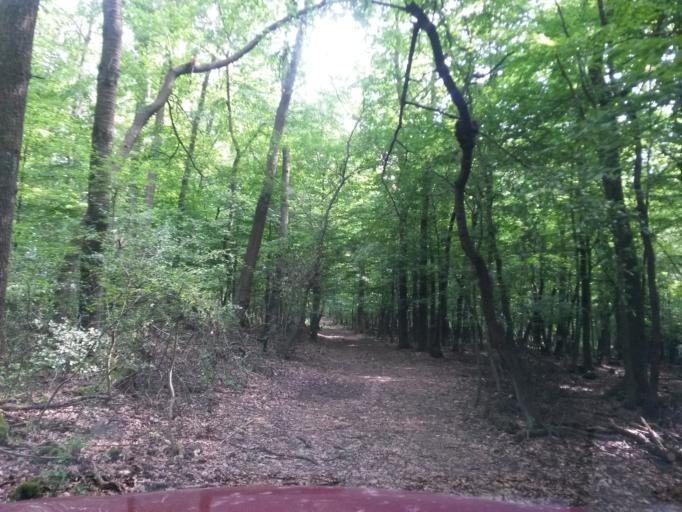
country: SK
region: Kosicky
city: Moldava nad Bodvou
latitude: 48.6324
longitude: 21.1018
